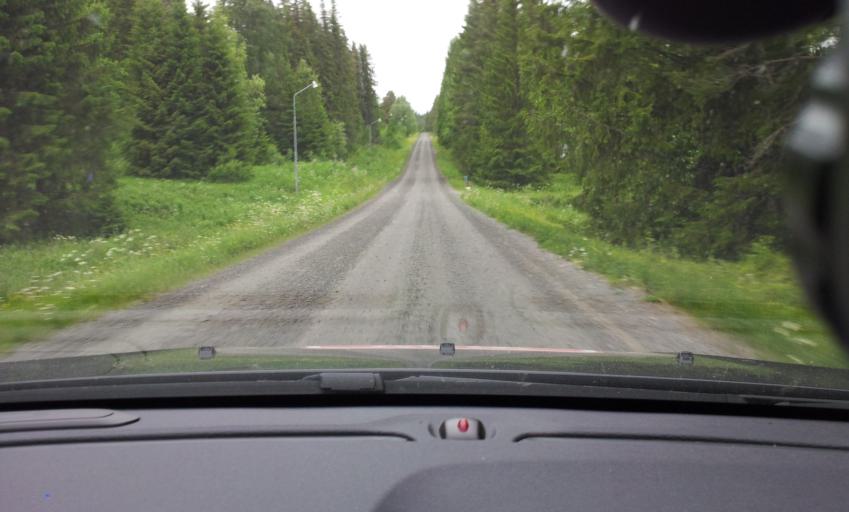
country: SE
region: Jaemtland
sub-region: Krokoms Kommun
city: Valla
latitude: 63.2610
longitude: 13.9231
